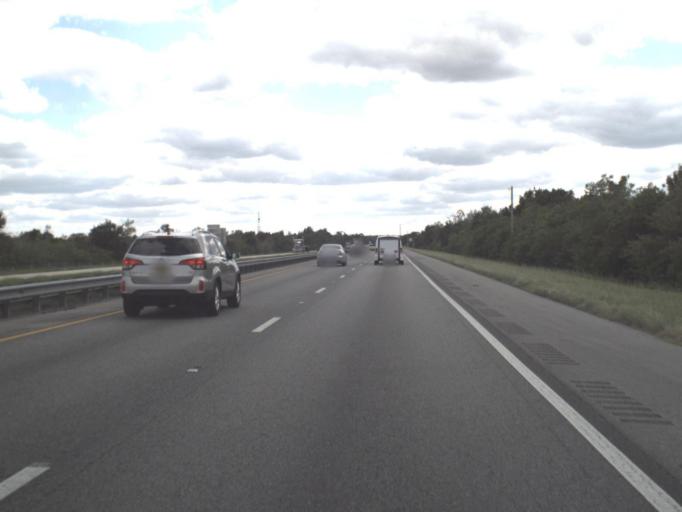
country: US
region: Florida
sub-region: Osceola County
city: Saint Cloud
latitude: 28.2456
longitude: -81.3280
